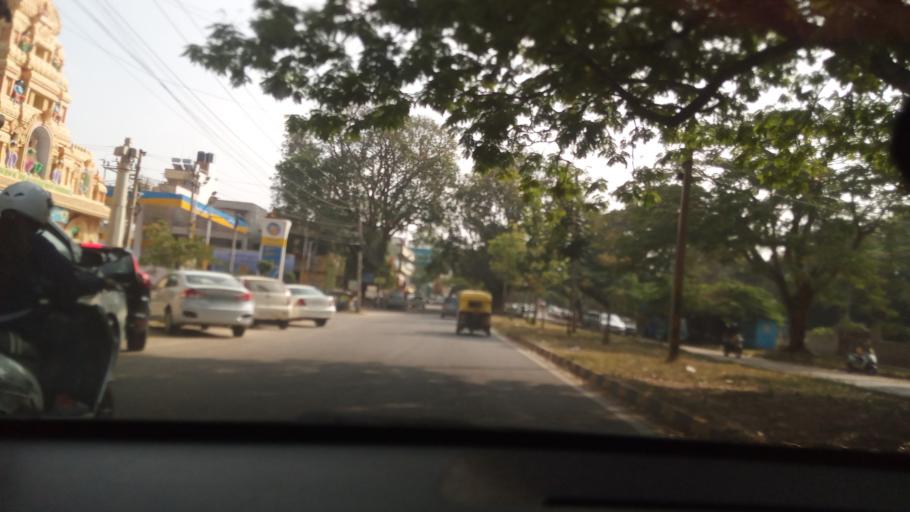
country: IN
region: Karnataka
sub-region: Mysore
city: Mysore
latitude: 12.2958
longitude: 76.6258
